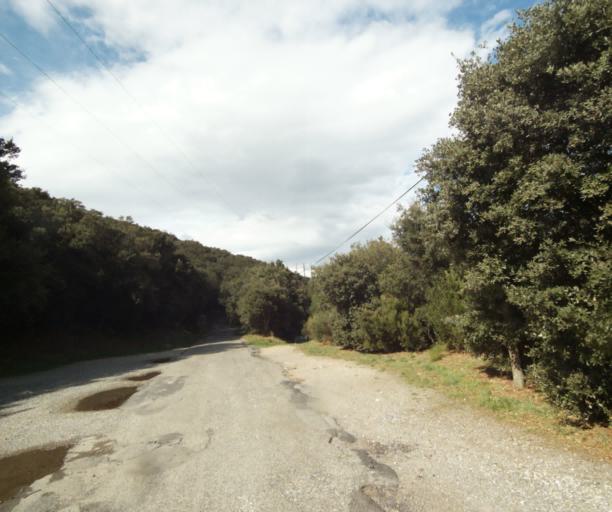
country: FR
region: Languedoc-Roussillon
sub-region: Departement des Pyrenees-Orientales
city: Sorede
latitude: 42.5146
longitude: 2.9884
